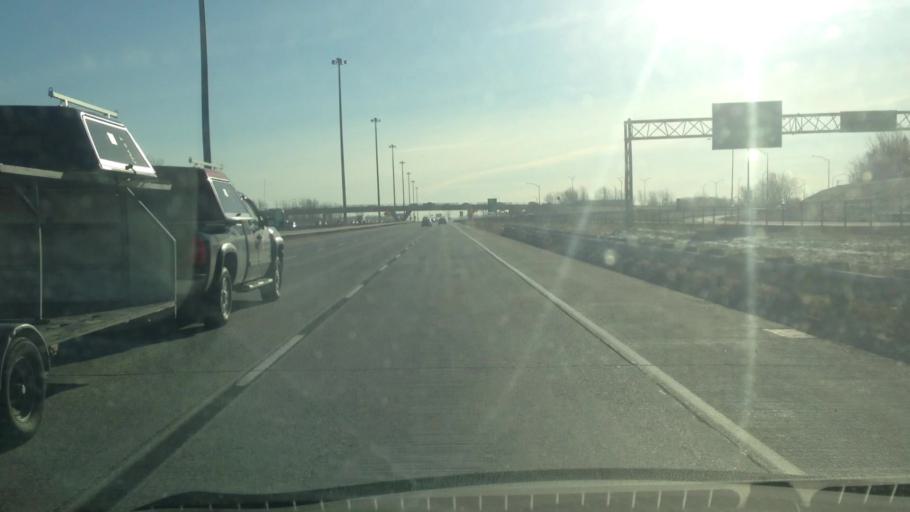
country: CA
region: Quebec
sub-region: Laurentides
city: Boisbriand
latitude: 45.5698
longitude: -73.8254
